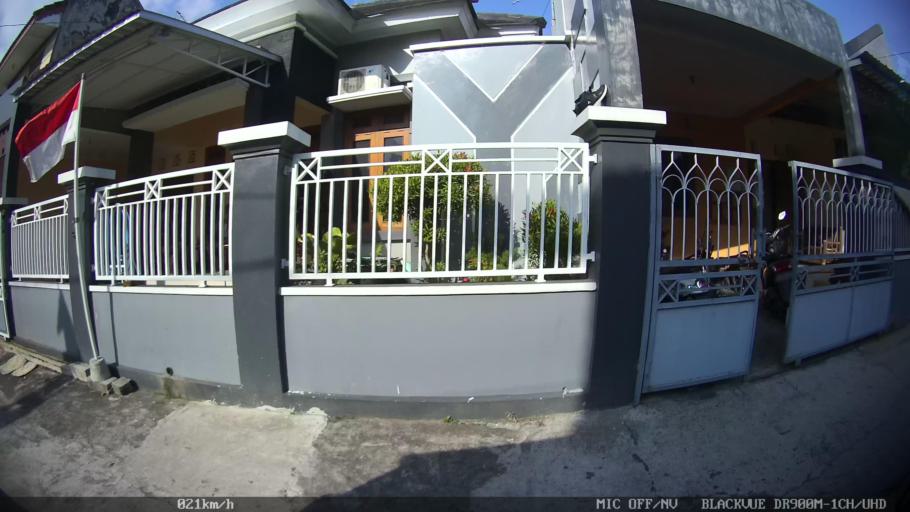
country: ID
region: Daerah Istimewa Yogyakarta
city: Yogyakarta
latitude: -7.8205
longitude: 110.3795
